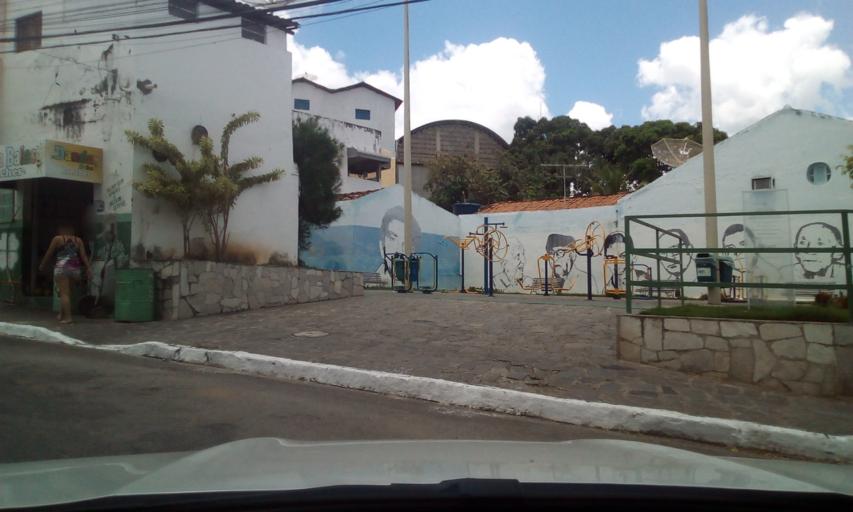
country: BR
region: Paraiba
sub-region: Guarabira
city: Guarabira
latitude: -6.8550
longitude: -35.4878
